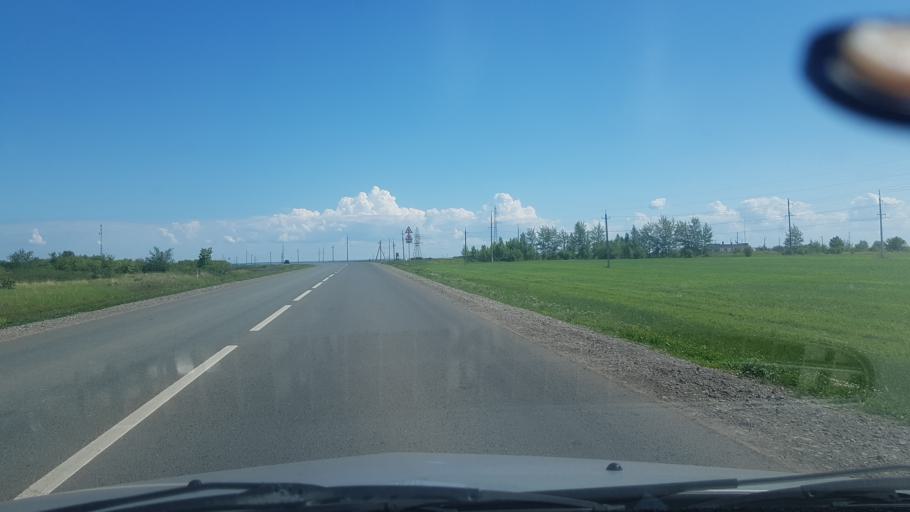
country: RU
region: Tatarstan
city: Nurlat
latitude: 54.4447
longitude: 50.8198
